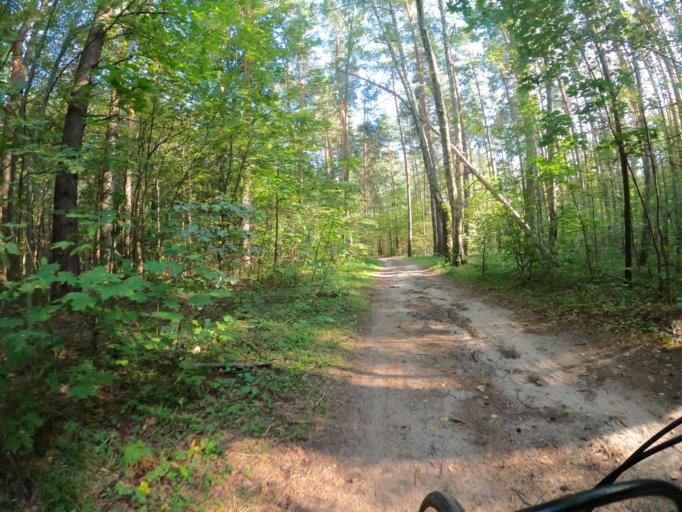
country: RU
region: Moskovskaya
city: Stupino
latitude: 54.8705
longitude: 38.0994
